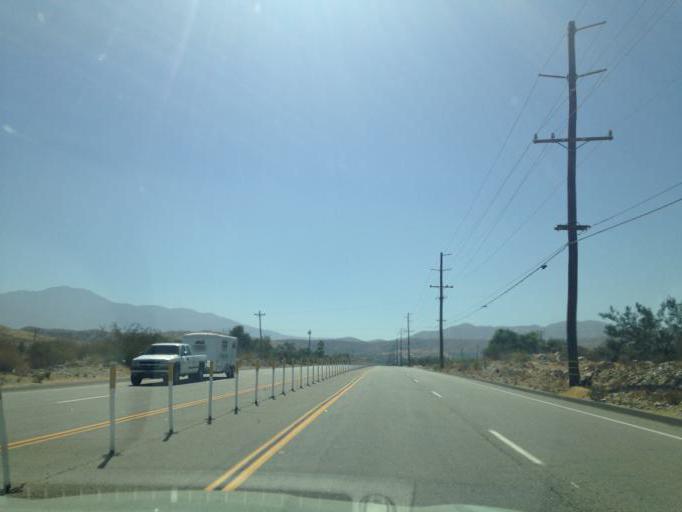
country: US
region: California
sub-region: San Bernardino County
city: Morongo Valley
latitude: 34.0679
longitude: -116.5538
